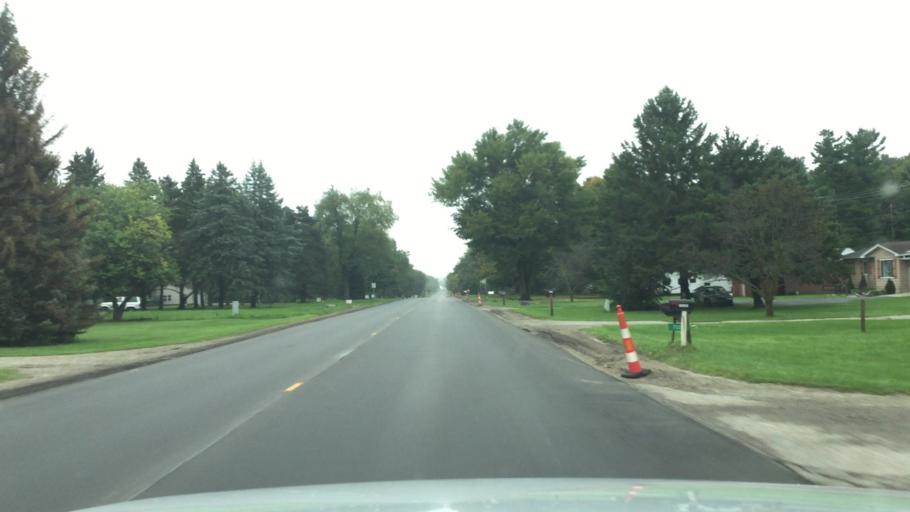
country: US
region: Michigan
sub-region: Shiawassee County
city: Perry
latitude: 42.8902
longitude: -84.2219
